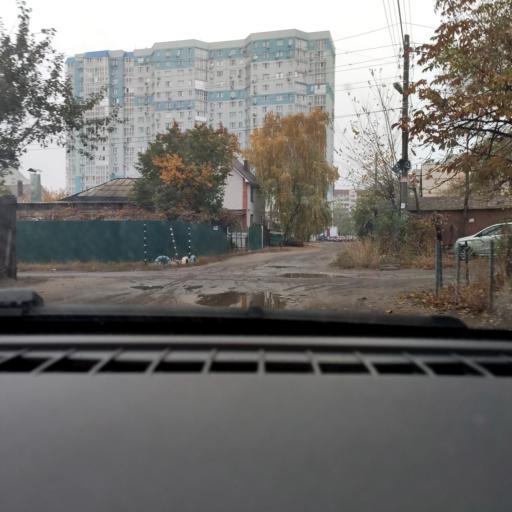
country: RU
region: Voronezj
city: Voronezh
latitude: 51.6524
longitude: 39.2375
